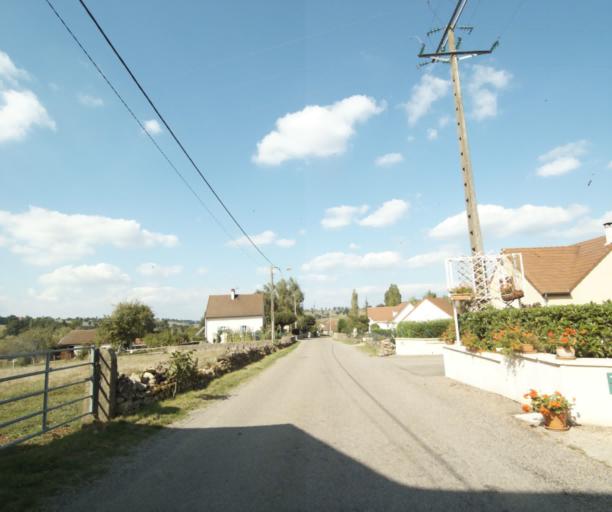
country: FR
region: Bourgogne
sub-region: Departement de Saone-et-Loire
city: Charolles
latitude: 46.3632
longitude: 4.2342
